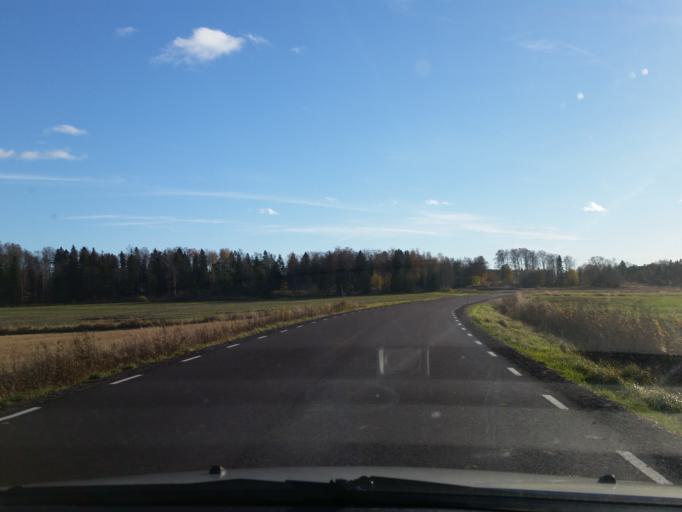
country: AX
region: Alands landsbygd
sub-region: Jomala
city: Jomala
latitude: 60.1939
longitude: 19.9595
